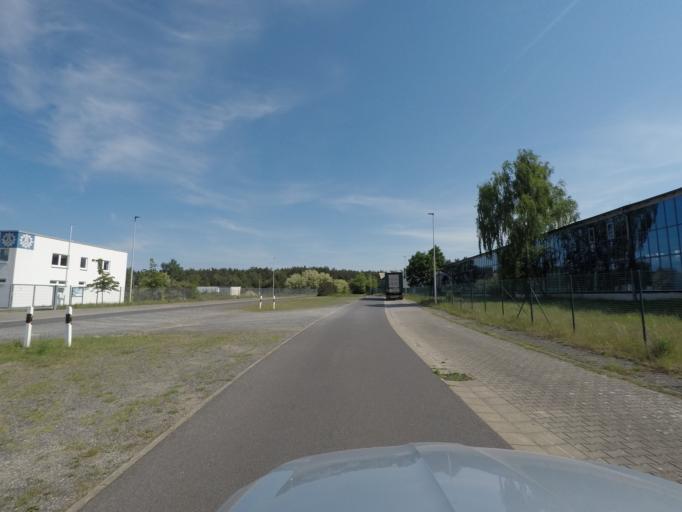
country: DE
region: Brandenburg
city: Britz
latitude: 52.8560
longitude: 13.7662
